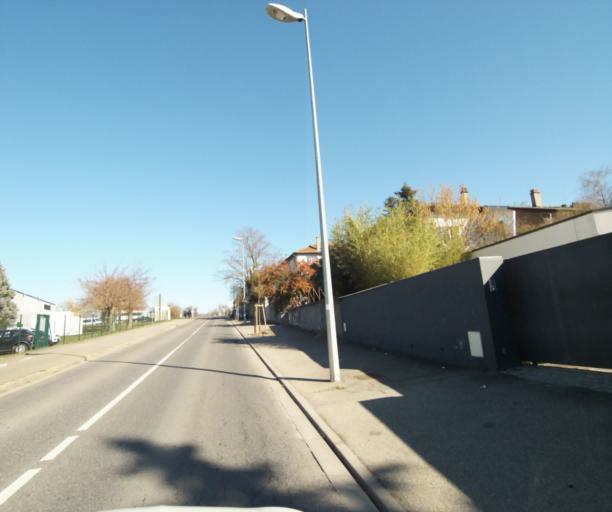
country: FR
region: Lorraine
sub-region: Departement de Meurthe-et-Moselle
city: Malzeville
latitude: 48.7254
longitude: 6.1816
